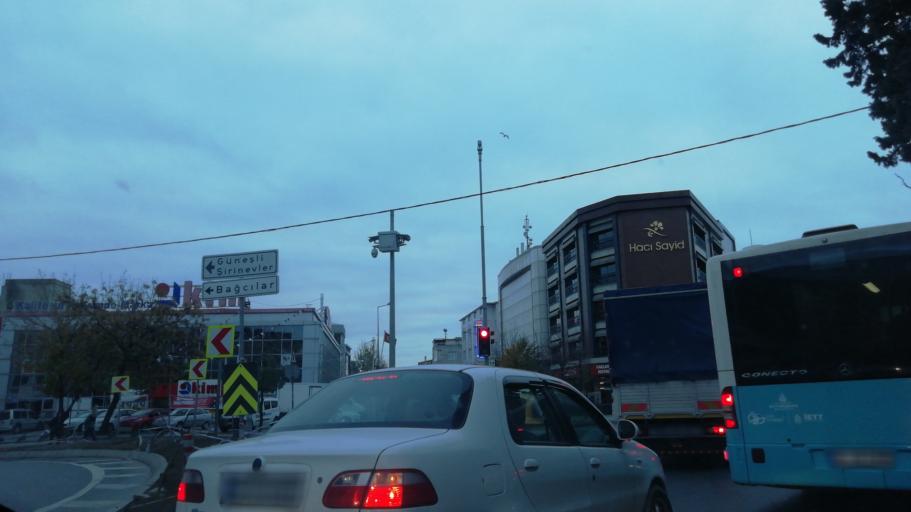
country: TR
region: Istanbul
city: Bahcelievler
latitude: 41.0137
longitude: 28.8250
